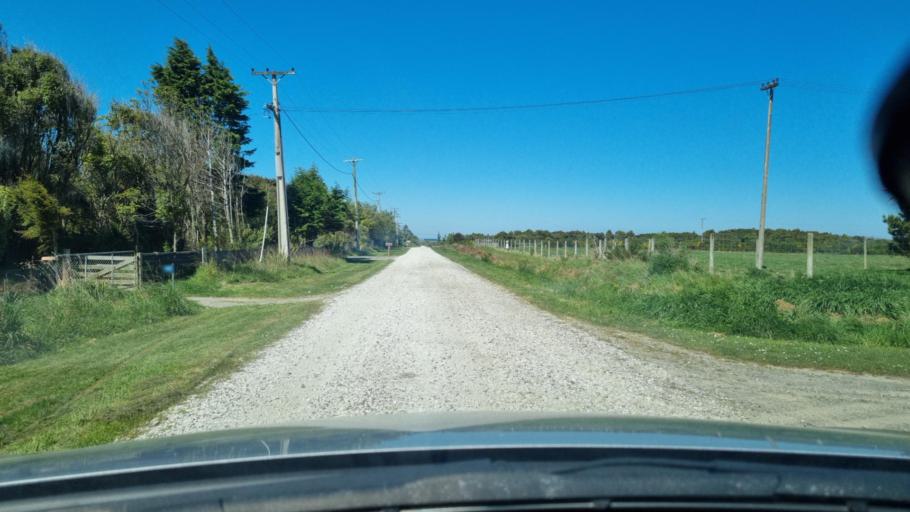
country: NZ
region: Southland
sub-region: Invercargill City
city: Invercargill
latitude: -46.4492
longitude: 168.3166
